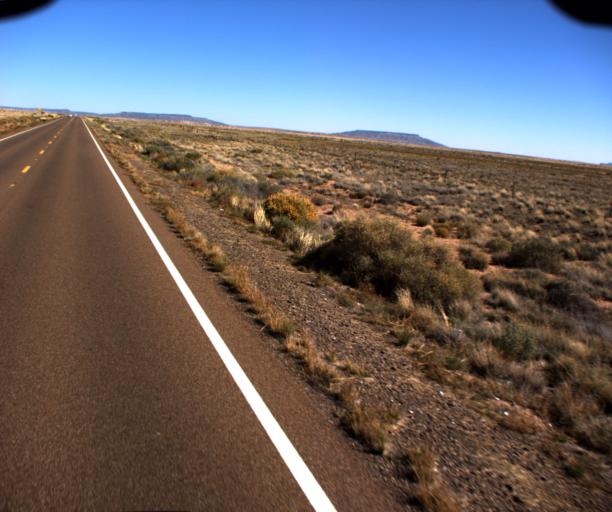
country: US
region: Arizona
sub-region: Navajo County
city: Joseph City
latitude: 35.1498
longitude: -110.4723
